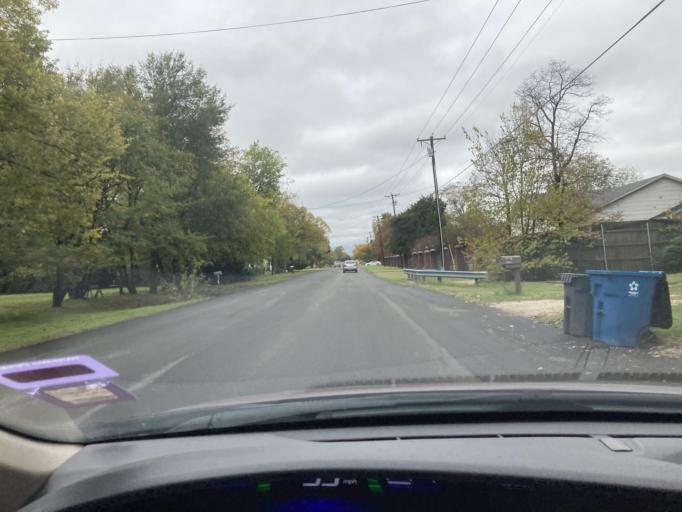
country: US
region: Texas
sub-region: Navarro County
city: Corsicana
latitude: 32.0830
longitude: -96.4966
